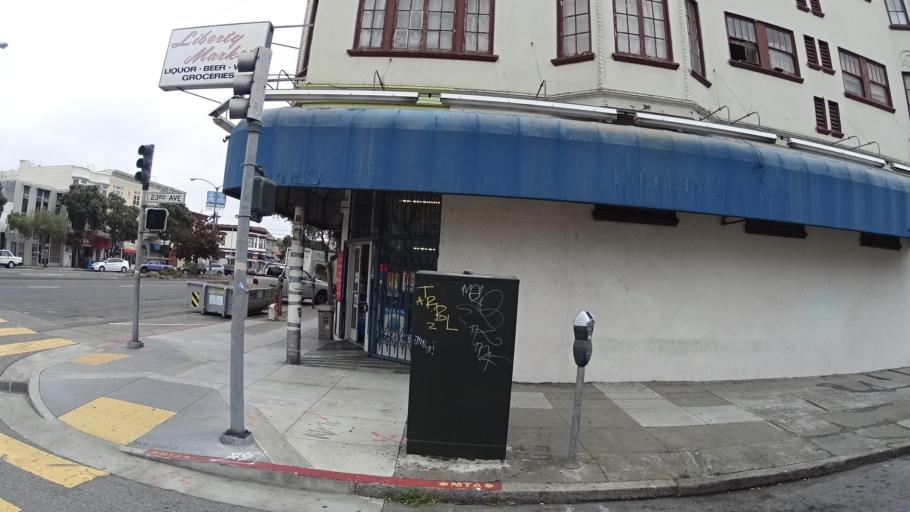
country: US
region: California
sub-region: San Francisco County
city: San Francisco
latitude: 37.7800
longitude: -122.4826
